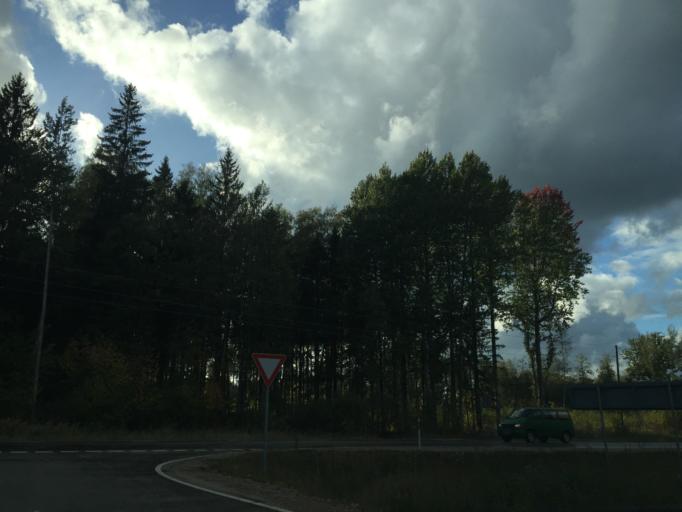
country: LV
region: Ligatne
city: Ligatne
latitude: 57.1388
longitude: 25.0823
